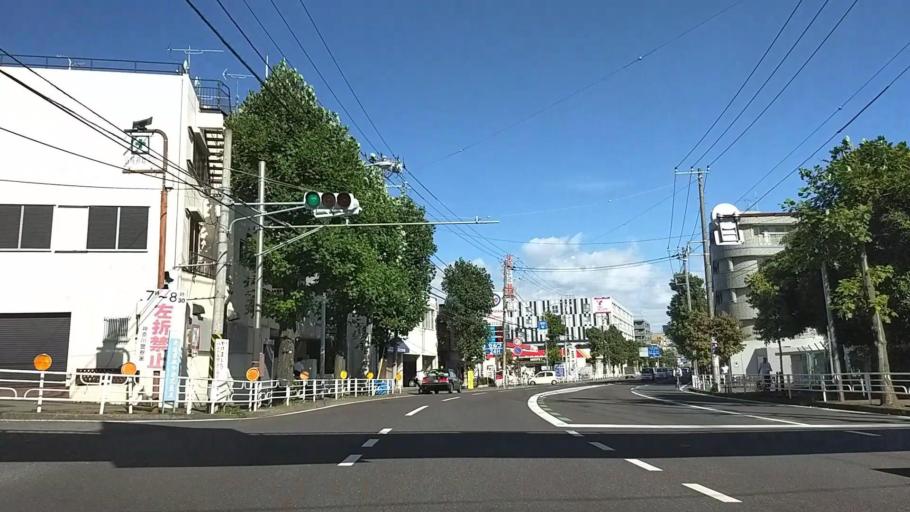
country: JP
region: Kanagawa
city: Yokohama
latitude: 35.4906
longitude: 139.6212
